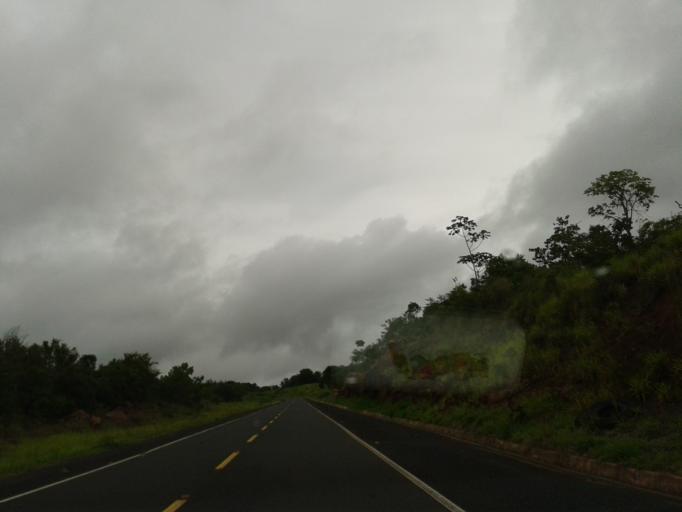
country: BR
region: Minas Gerais
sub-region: Santa Vitoria
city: Santa Vitoria
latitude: -19.2149
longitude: -50.0213
